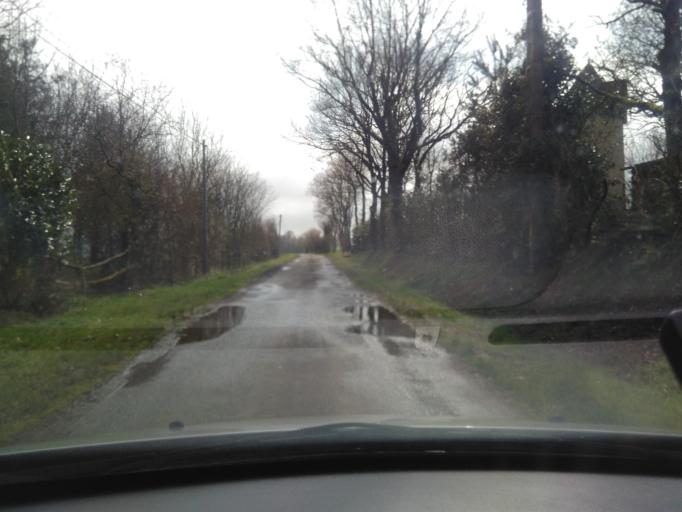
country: FR
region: Pays de la Loire
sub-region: Departement de la Vendee
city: Sainte-Cecile
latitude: 46.7076
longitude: -1.1322
